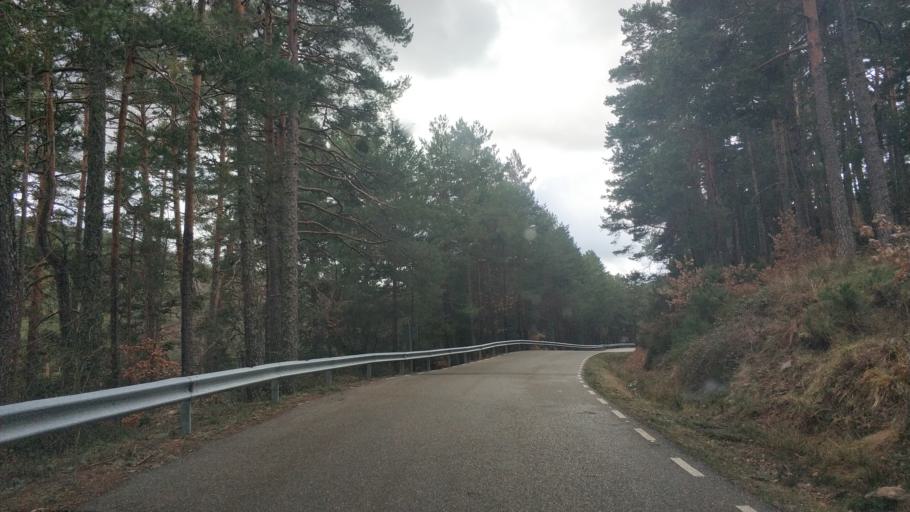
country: ES
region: Castille and Leon
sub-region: Provincia de Burgos
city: Quintanar de la Sierra
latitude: 42.0129
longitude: -3.0197
